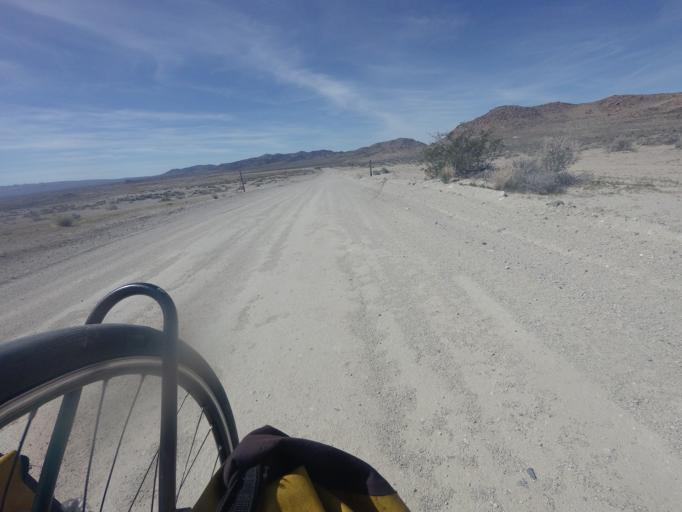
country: US
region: California
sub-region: San Bernardino County
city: Searles Valley
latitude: 35.6003
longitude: -117.3838
